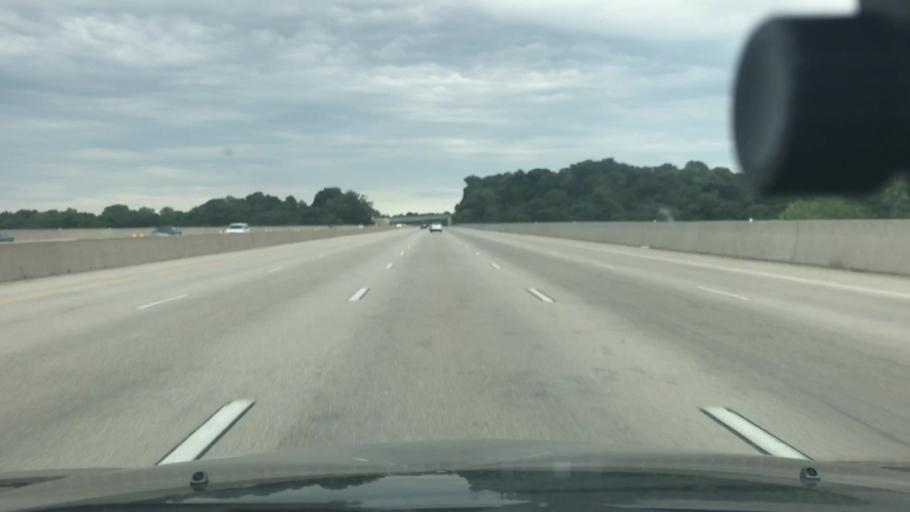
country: US
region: Missouri
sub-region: Saint Louis County
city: Maryland Heights
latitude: 38.7062
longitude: -90.4881
